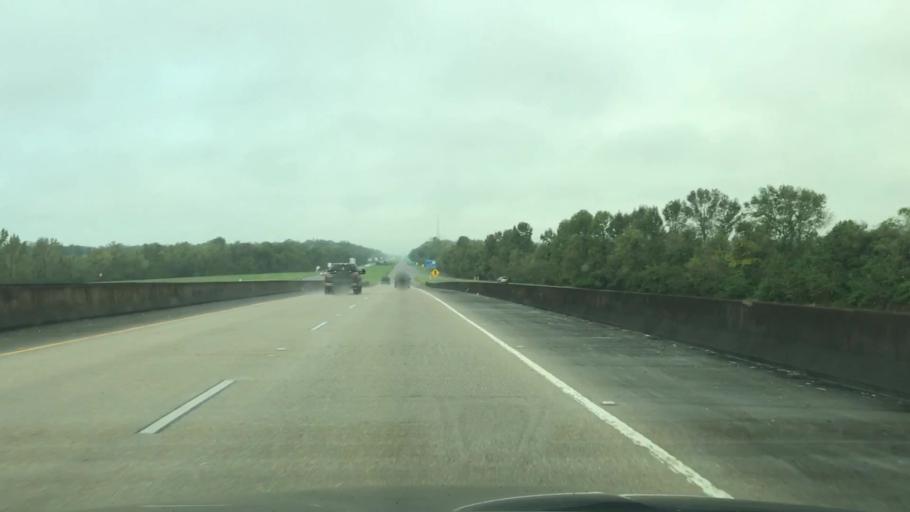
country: US
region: Louisiana
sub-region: Terrebonne Parish
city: Gray
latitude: 29.6826
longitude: -90.7525
